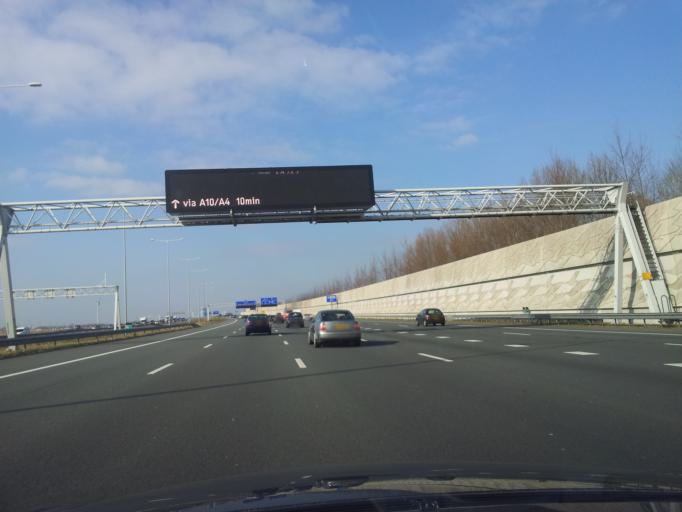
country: NL
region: North Holland
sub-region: Gemeente Amsterdam
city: Amsterdam-Zuidoost
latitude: 52.2715
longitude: 4.9592
